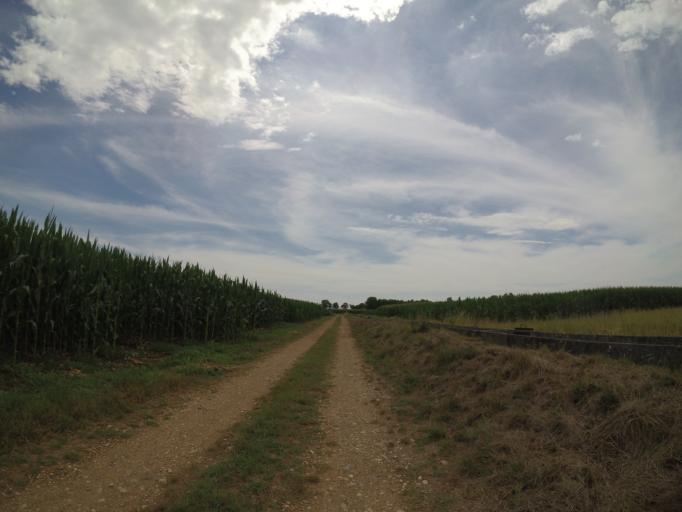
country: IT
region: Friuli Venezia Giulia
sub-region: Provincia di Udine
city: Bertiolo
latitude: 45.9595
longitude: 13.0583
